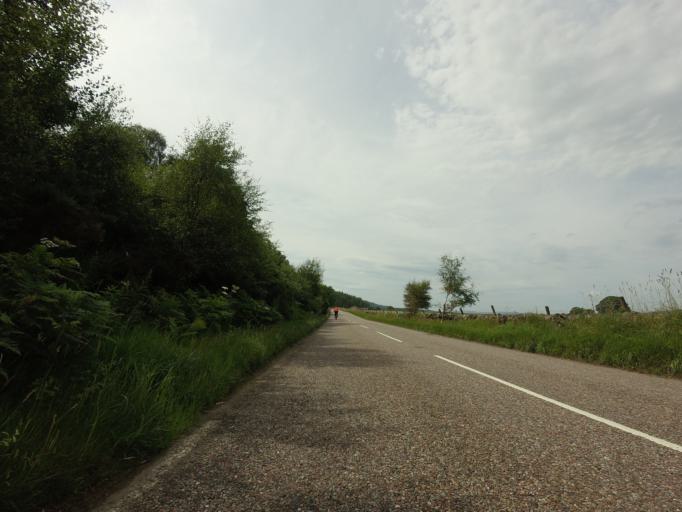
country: GB
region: Scotland
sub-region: Highland
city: Alness
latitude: 57.8498
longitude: -4.2768
